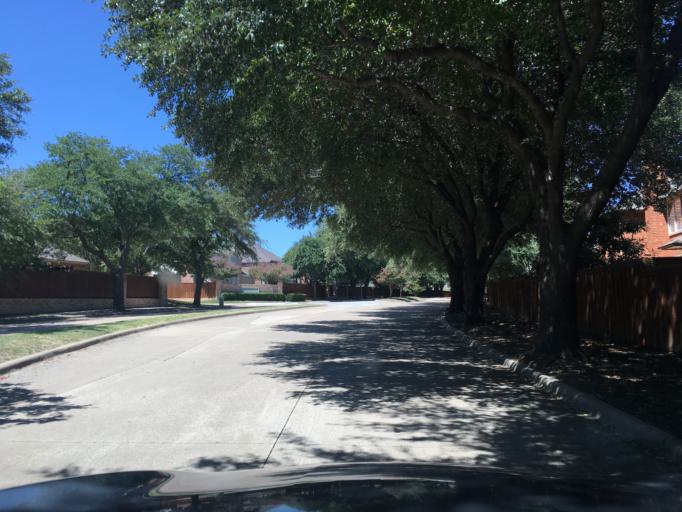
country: US
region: Texas
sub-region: Dallas County
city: Sachse
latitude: 32.9652
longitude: -96.6283
